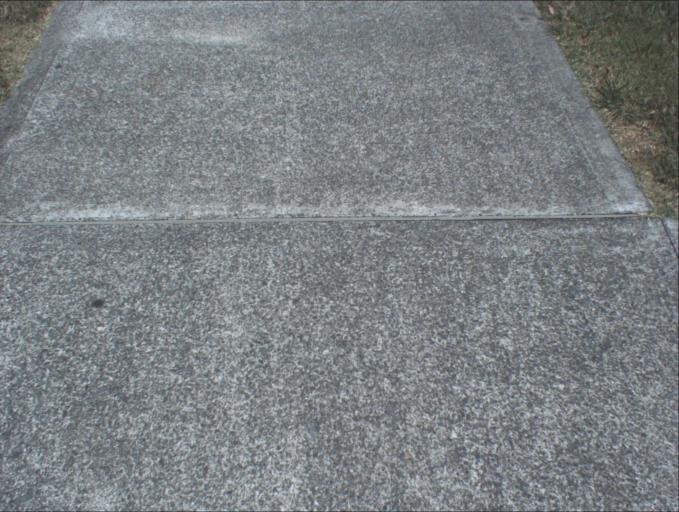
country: AU
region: Queensland
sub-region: Logan
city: Windaroo
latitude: -27.7433
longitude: 153.1928
